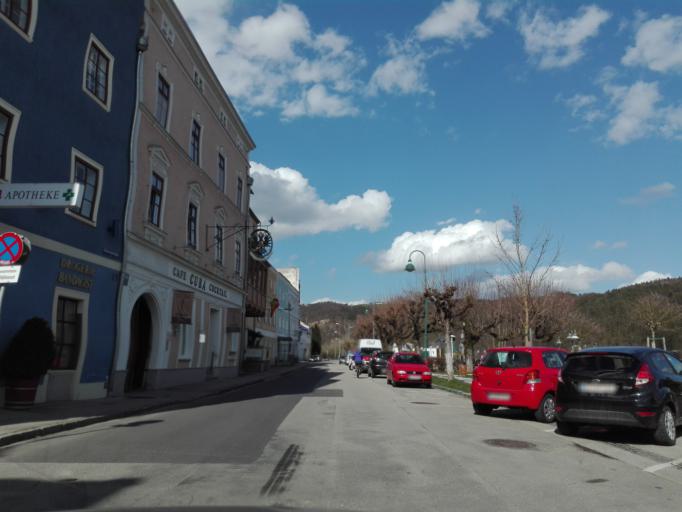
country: AT
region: Upper Austria
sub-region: Politischer Bezirk Urfahr-Umgebung
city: Feldkirchen an der Donau
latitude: 48.3686
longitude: 14.0263
